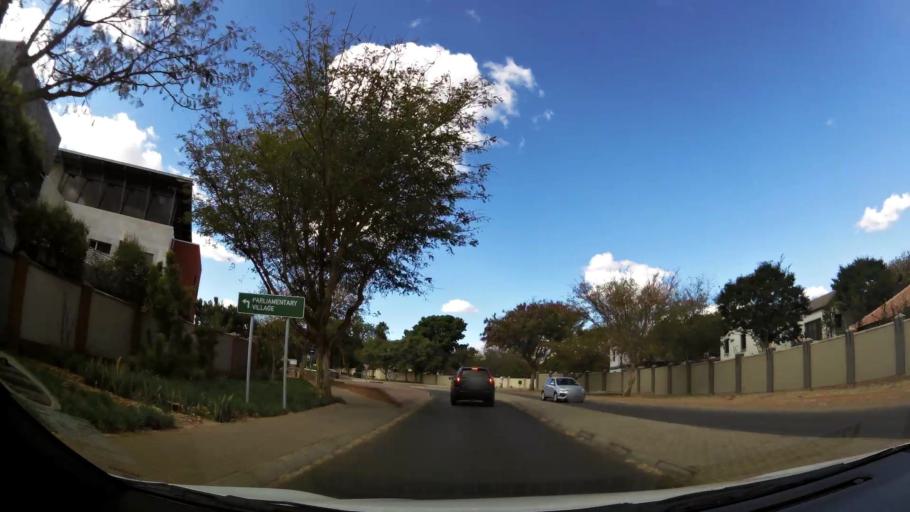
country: ZA
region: Limpopo
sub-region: Capricorn District Municipality
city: Polokwane
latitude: -23.8913
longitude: 29.4755
